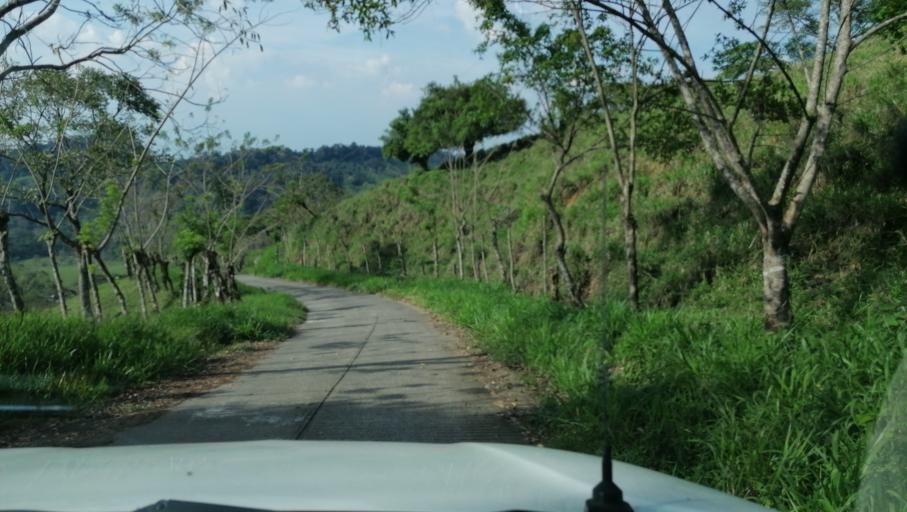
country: MX
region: Chiapas
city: Ostuacan
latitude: 17.4648
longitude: -93.2334
